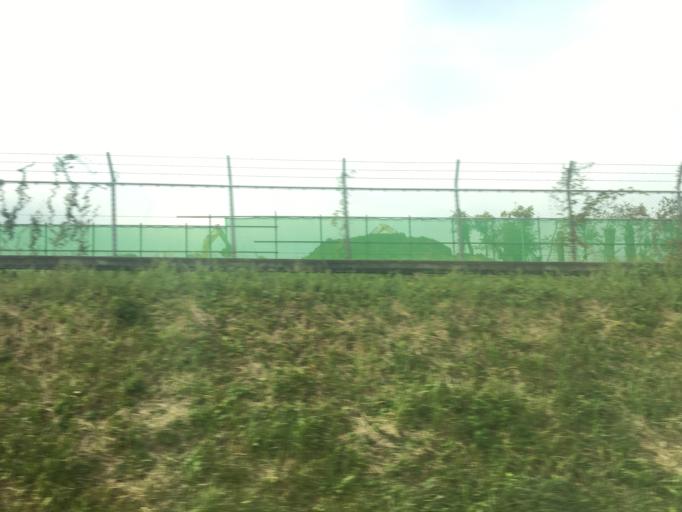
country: JP
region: Saitama
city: Sayama
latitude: 35.8437
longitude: 139.4191
